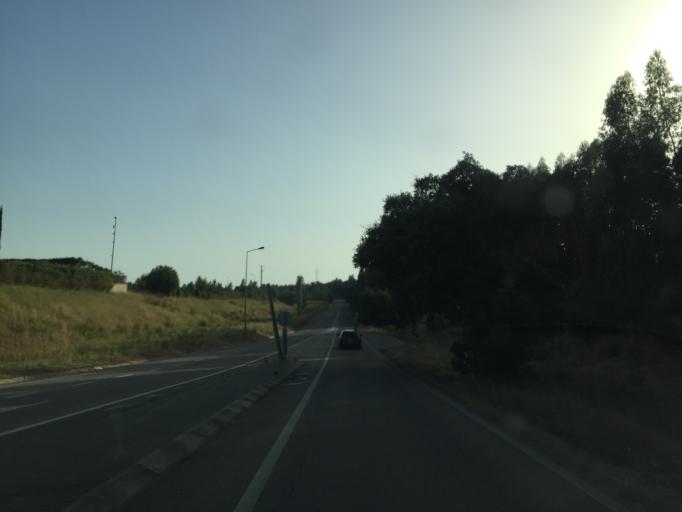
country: PT
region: Santarem
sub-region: Entroncamento
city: Entroncamento
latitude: 39.5009
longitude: -8.4319
